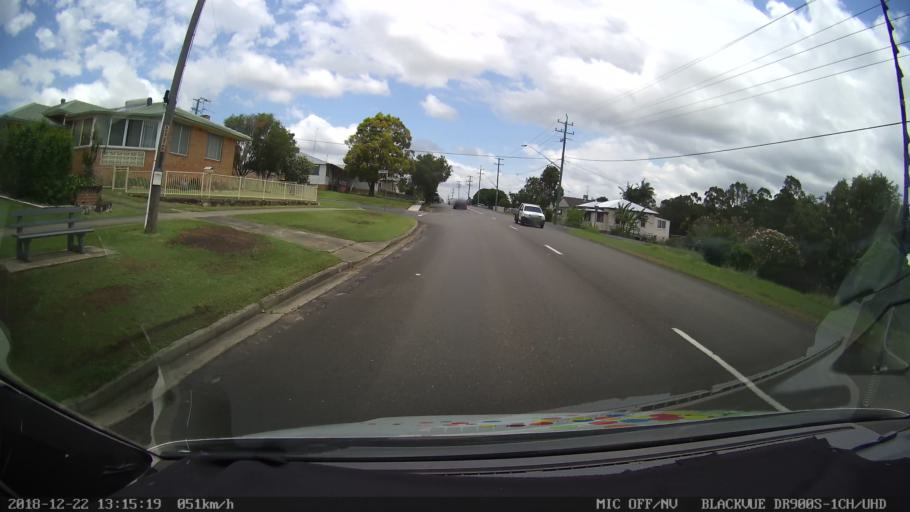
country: AU
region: New South Wales
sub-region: Clarence Valley
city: South Grafton
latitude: -29.7170
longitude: 152.9392
